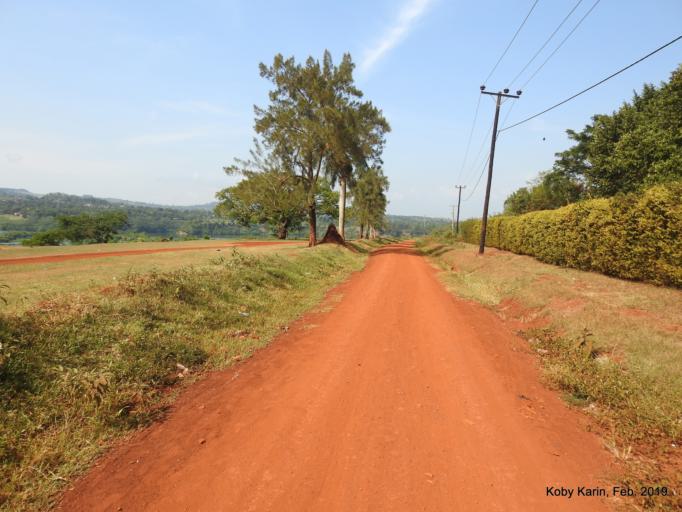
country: UG
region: Eastern Region
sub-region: Jinja District
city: Jinja
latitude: 0.4843
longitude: 33.1622
